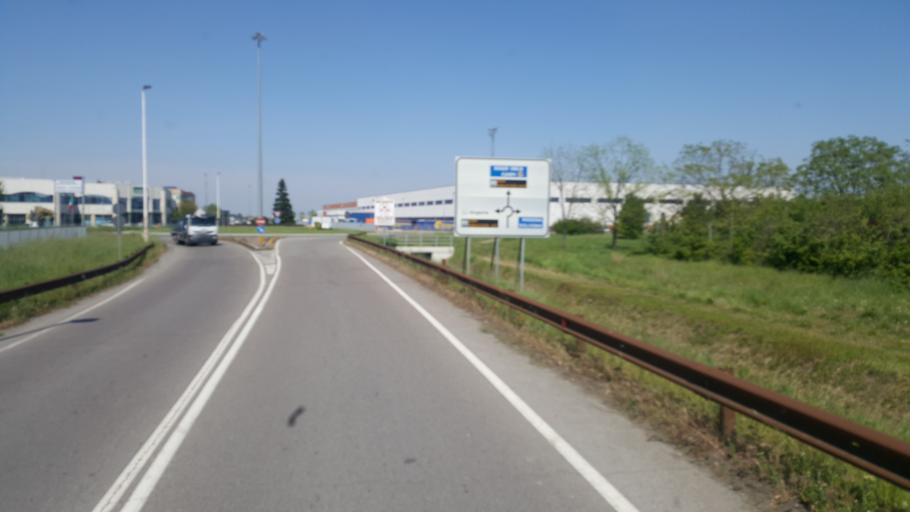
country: IT
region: Emilia-Romagna
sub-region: Provincia di Modena
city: Campogalliano
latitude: 44.6829
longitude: 10.8572
